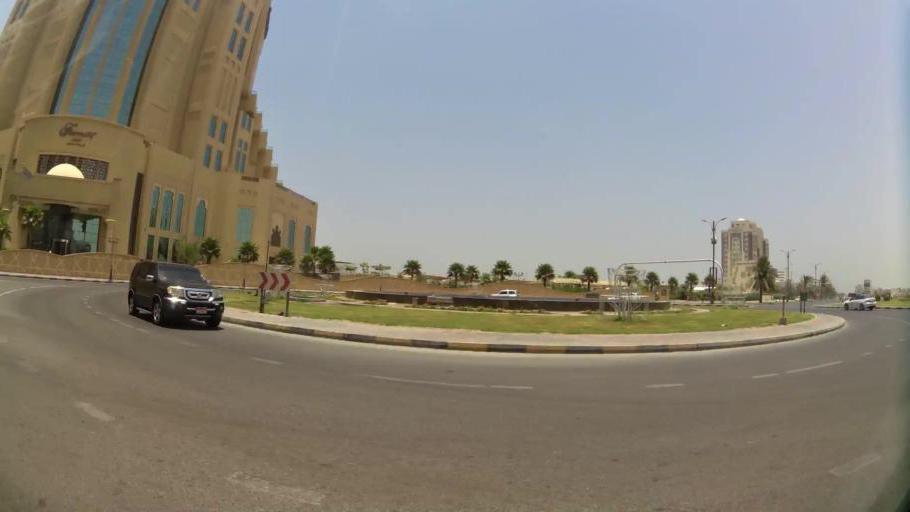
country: AE
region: Ajman
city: Ajman
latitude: 25.4176
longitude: 55.4402
